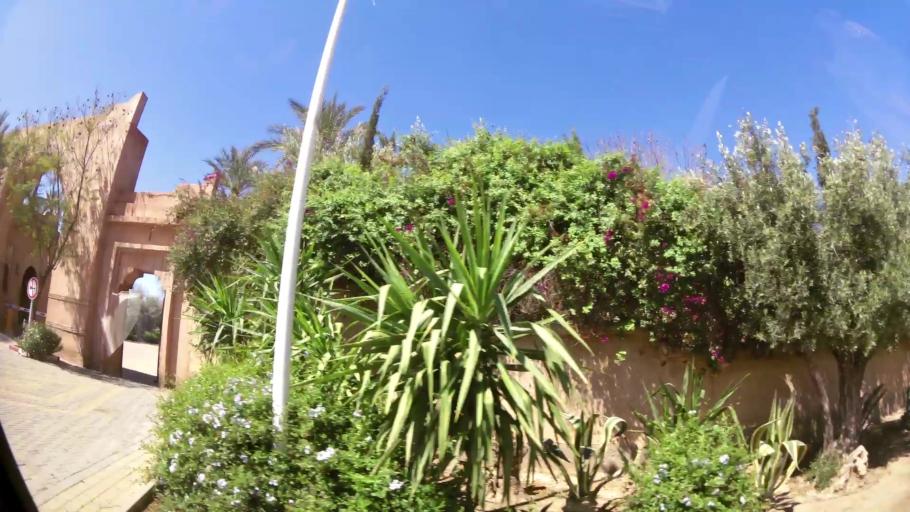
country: MA
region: Marrakech-Tensift-Al Haouz
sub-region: Marrakech
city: Marrakesh
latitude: 31.6751
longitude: -7.9858
